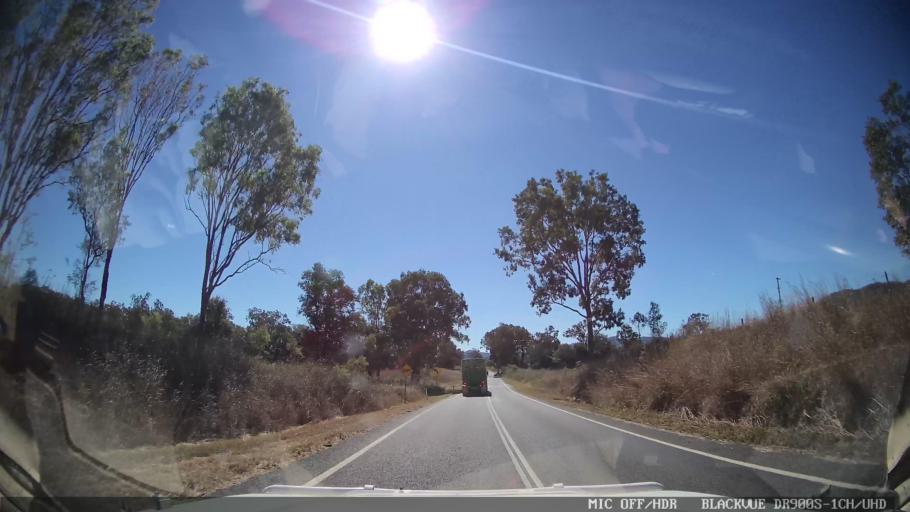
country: AU
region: Queensland
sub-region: Gladstone
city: Toolooa
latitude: -24.2761
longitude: 151.2762
